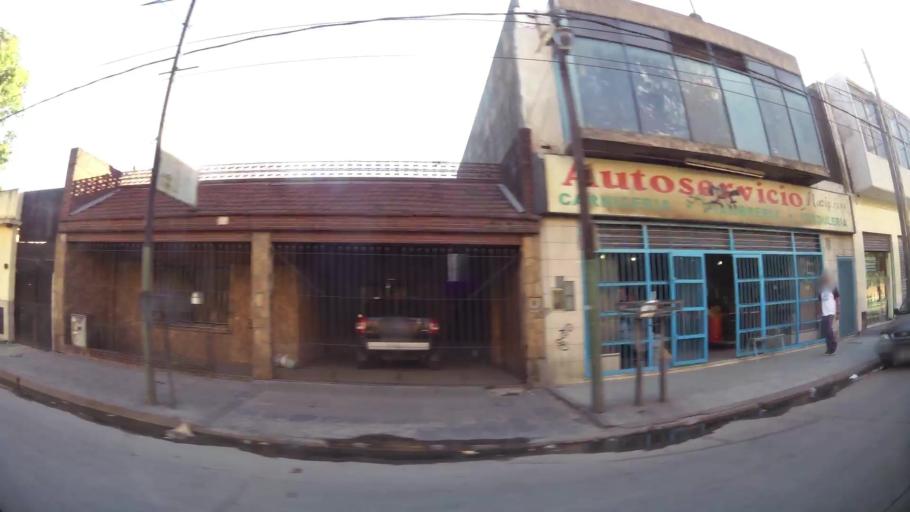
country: AR
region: Buenos Aires
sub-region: Partido de Almirante Brown
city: Adrogue
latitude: -34.7519
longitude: -58.3385
